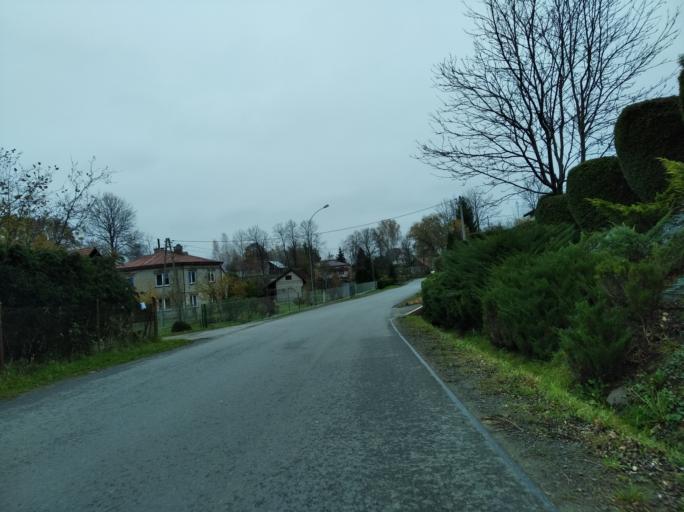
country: PL
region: Subcarpathian Voivodeship
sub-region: Powiat krosnienski
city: Jedlicze
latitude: 49.7351
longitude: 21.6525
